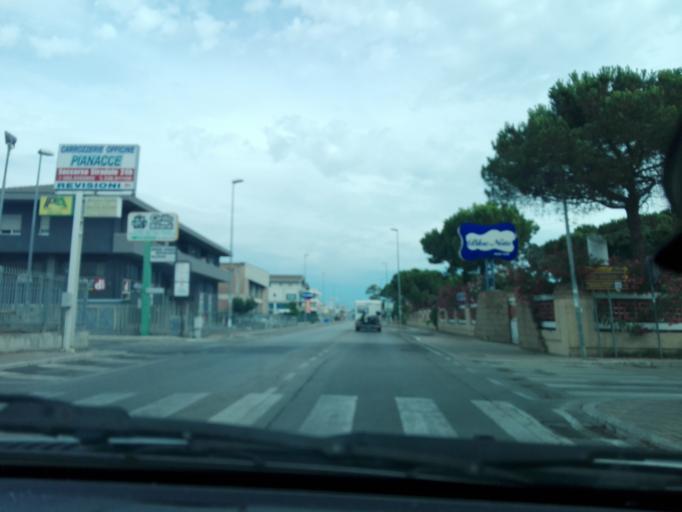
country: IT
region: Abruzzo
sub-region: Provincia di Pescara
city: San Martino Bassa
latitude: 42.5353
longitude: 14.1287
